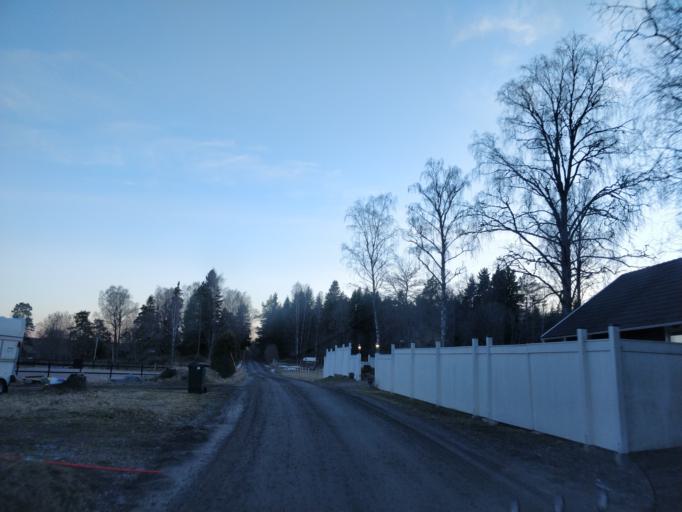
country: SE
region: Uppsala
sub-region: Enkopings Kommun
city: Orsundsbro
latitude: 59.8266
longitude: 17.1586
